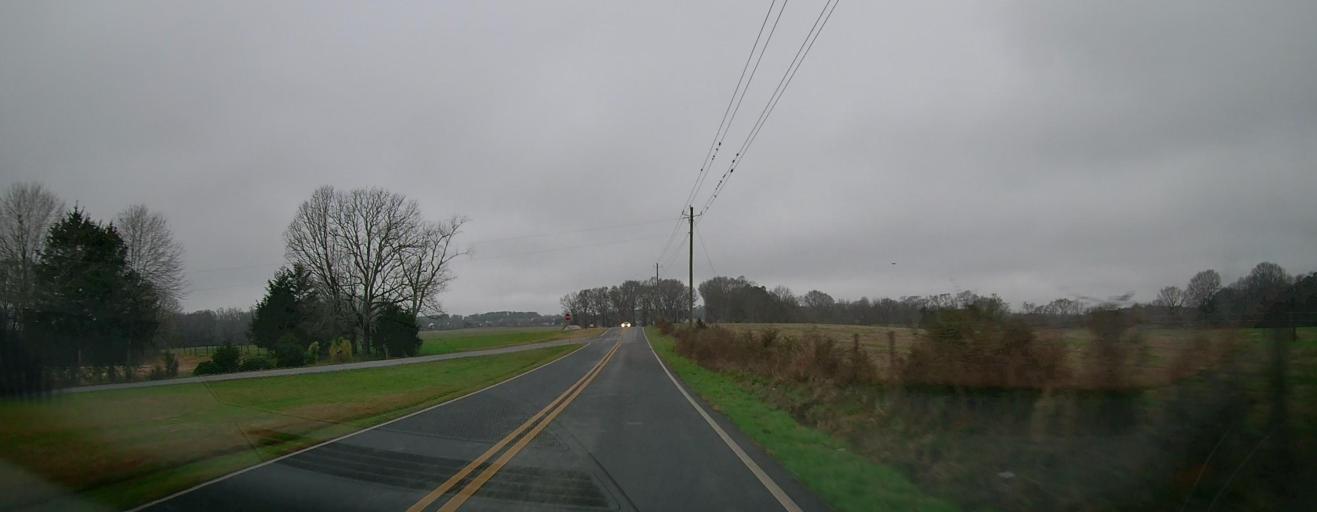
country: US
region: Georgia
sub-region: Pike County
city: Zebulon
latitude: 33.1544
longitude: -84.3536
